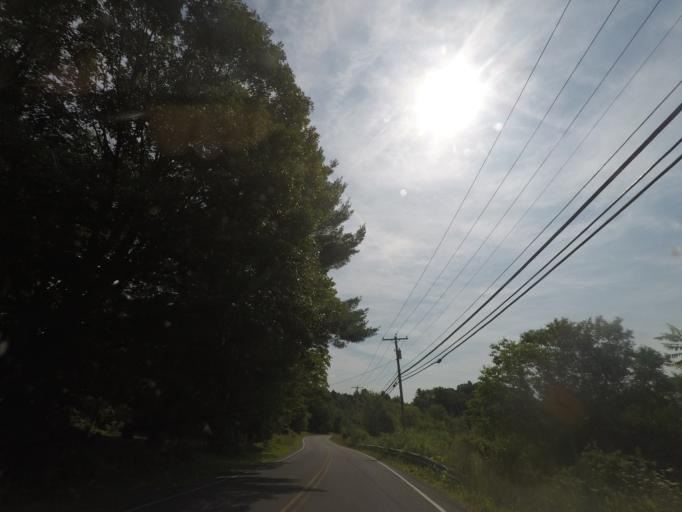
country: US
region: New York
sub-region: Rensselaer County
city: Wynantskill
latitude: 42.7058
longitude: -73.6185
